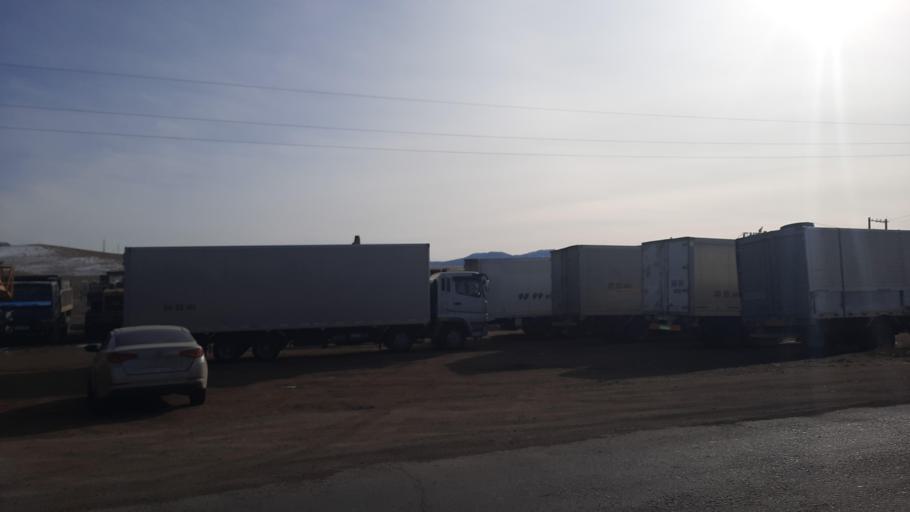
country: MN
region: Orhon
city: Erdenet
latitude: 49.0286
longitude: 104.0719
